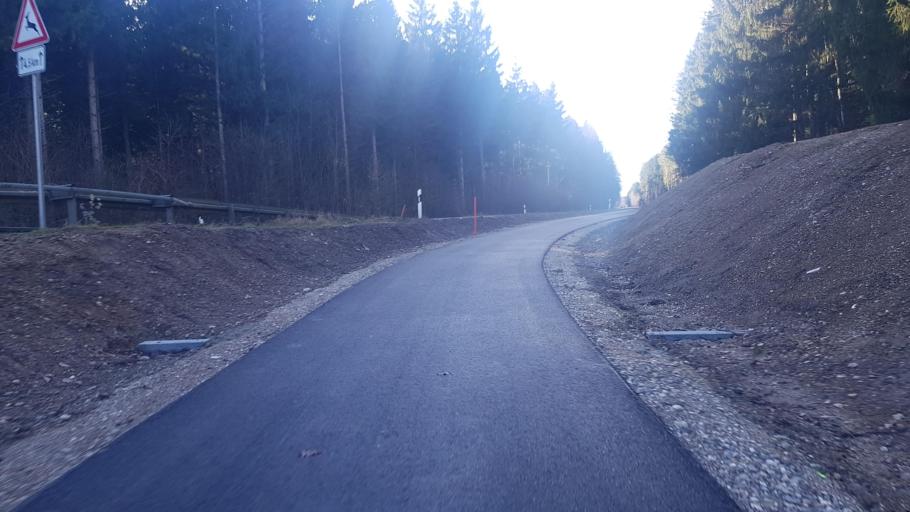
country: DE
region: Bavaria
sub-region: Upper Bavaria
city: Neuried
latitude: 48.0851
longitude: 11.4498
